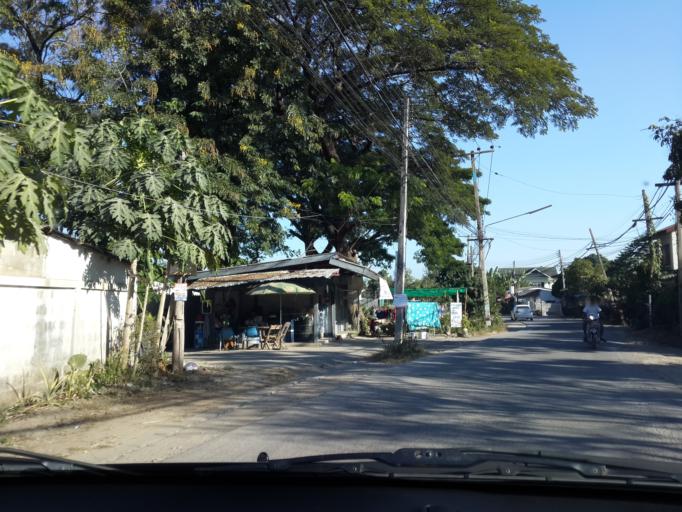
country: TH
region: Chiang Mai
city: Chiang Mai
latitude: 18.7462
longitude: 98.9432
